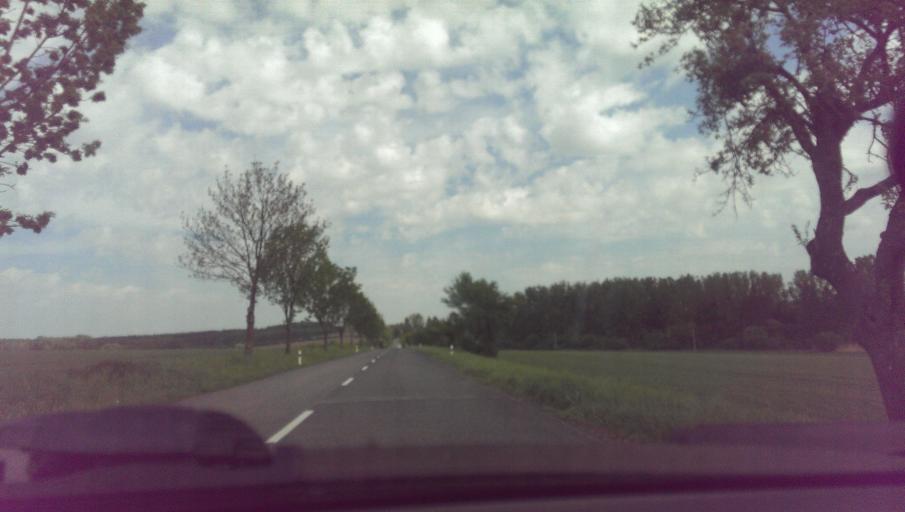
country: CZ
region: Zlin
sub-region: Okres Zlin
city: Otrokovice
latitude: 49.2269
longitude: 17.5360
